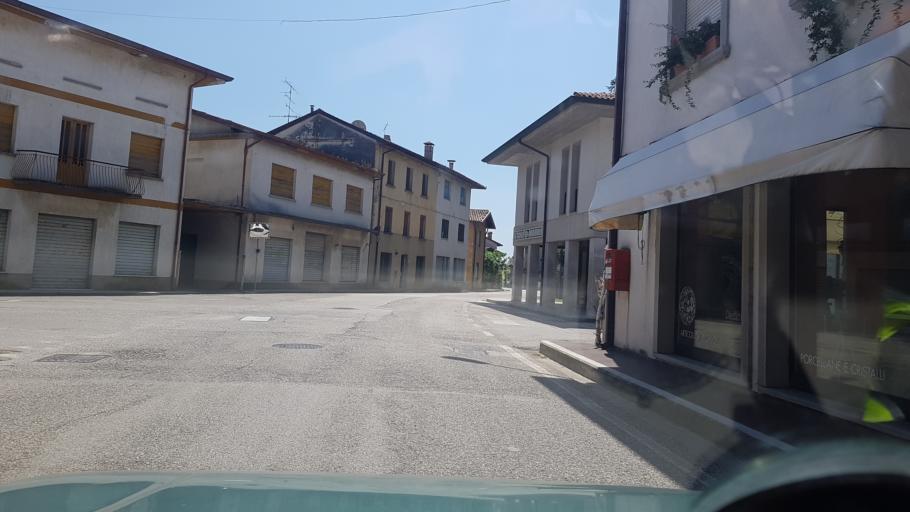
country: IT
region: Friuli Venezia Giulia
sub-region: Provincia di Udine
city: Nimis
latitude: 46.2073
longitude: 13.2667
